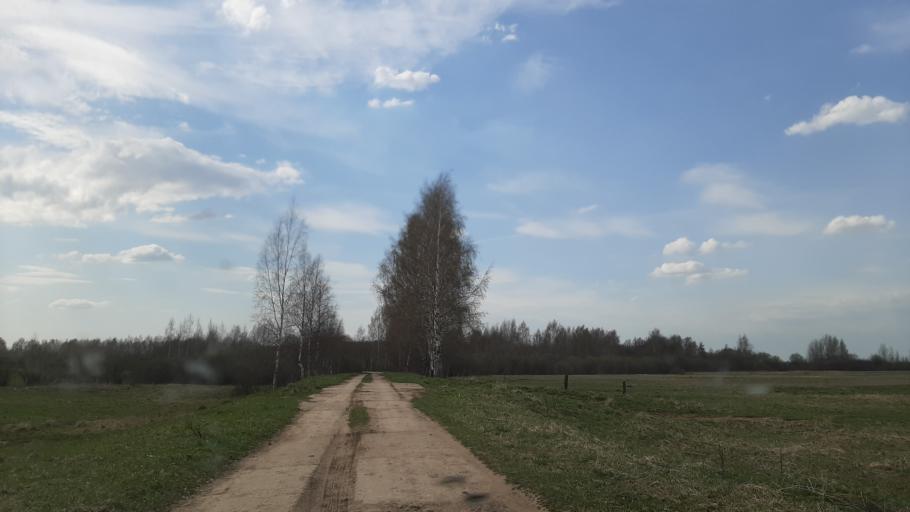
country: RU
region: Ivanovo
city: Privolzhsk
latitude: 57.3975
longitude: 41.3390
